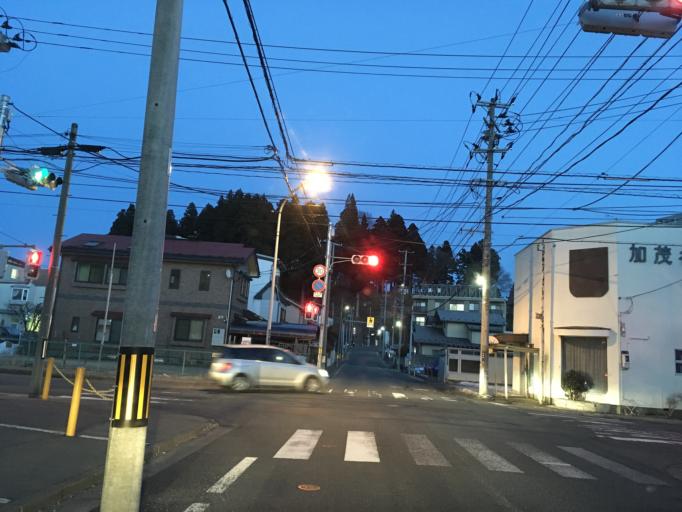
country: JP
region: Iwate
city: Morioka-shi
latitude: 39.7030
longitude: 141.1648
